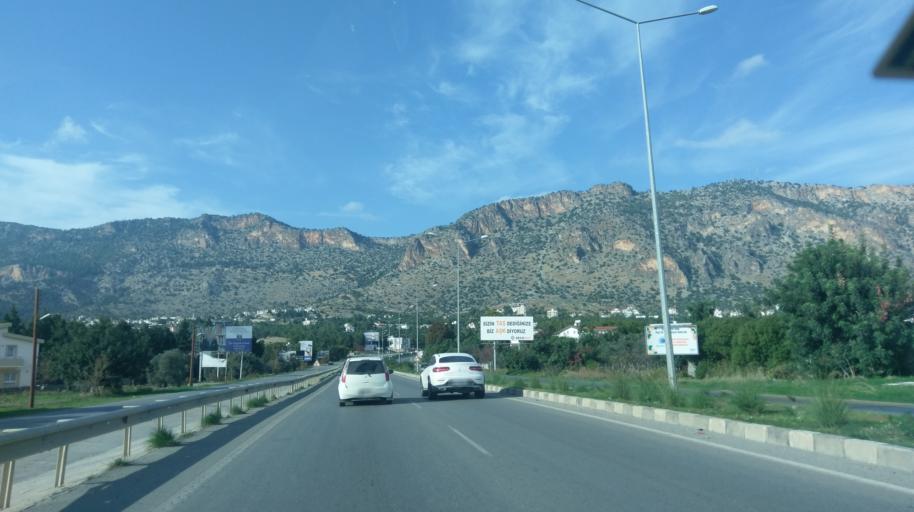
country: CY
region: Keryneia
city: Kyrenia
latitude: 35.2872
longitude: 33.2780
